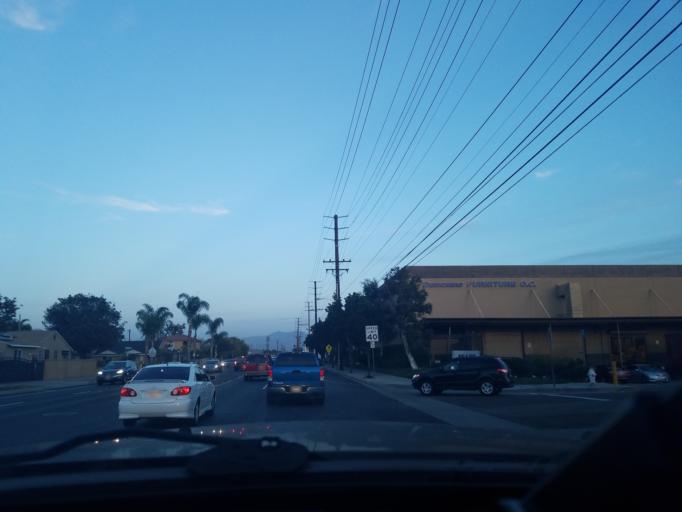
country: US
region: California
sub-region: Orange County
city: Santa Ana
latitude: 33.7160
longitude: -117.8749
